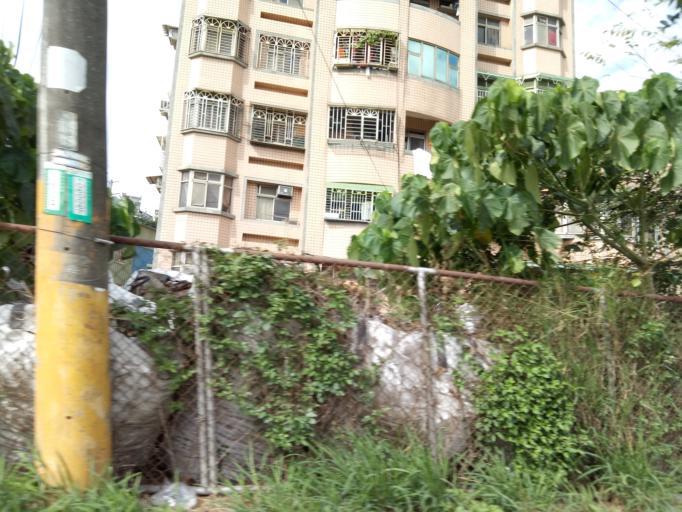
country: TW
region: Taiwan
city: Daxi
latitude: 24.8968
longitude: 121.2884
